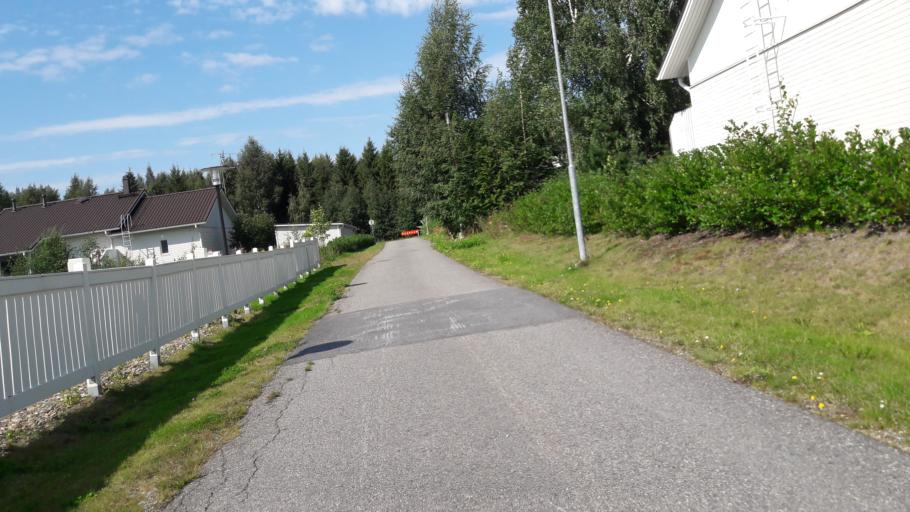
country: FI
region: North Karelia
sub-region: Joensuu
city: Joensuu
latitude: 62.5397
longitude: 29.8417
